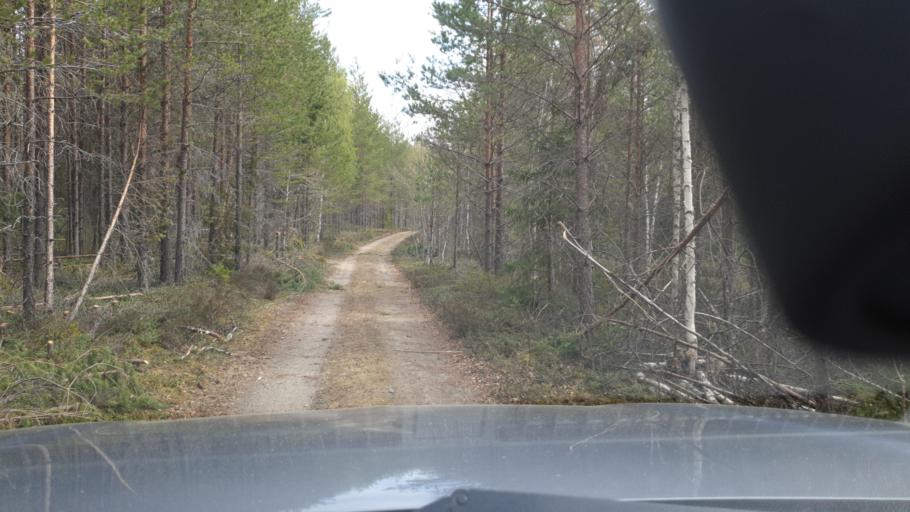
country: SE
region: Vaesternorrland
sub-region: Ange Kommun
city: Ange
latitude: 62.1873
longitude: 15.6138
